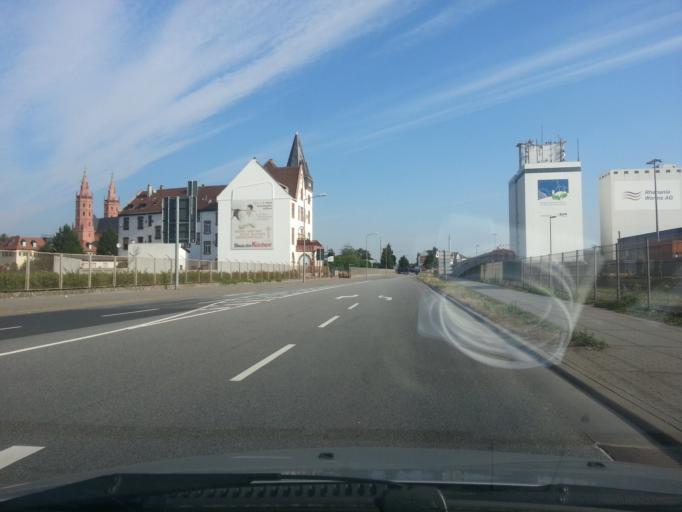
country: DE
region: Rheinland-Pfalz
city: Worms
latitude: 49.6370
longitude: 8.3709
